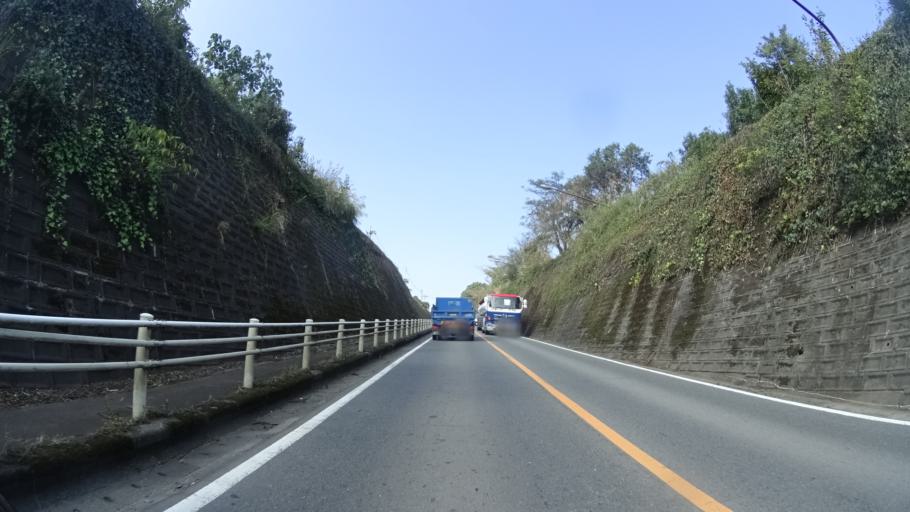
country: JP
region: Kumamoto
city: Ozu
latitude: 32.8360
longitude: 130.8545
